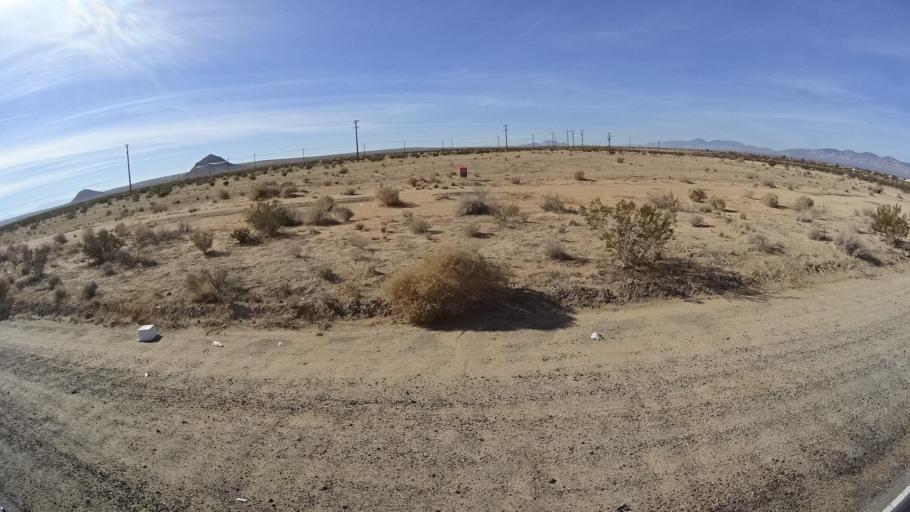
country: US
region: California
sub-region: Kern County
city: California City
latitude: 35.1127
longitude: -117.9309
